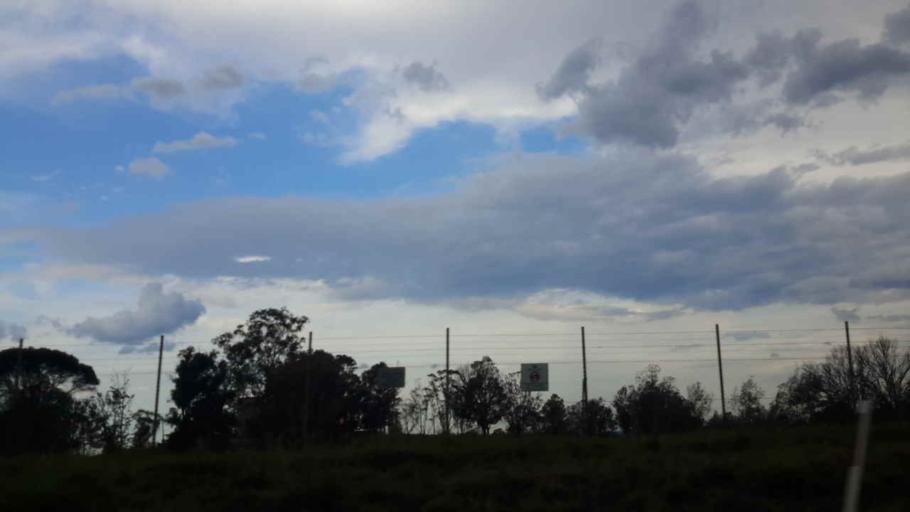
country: AU
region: New South Wales
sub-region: Penrith Municipality
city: Glenmore Park
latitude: -33.8165
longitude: 150.6886
